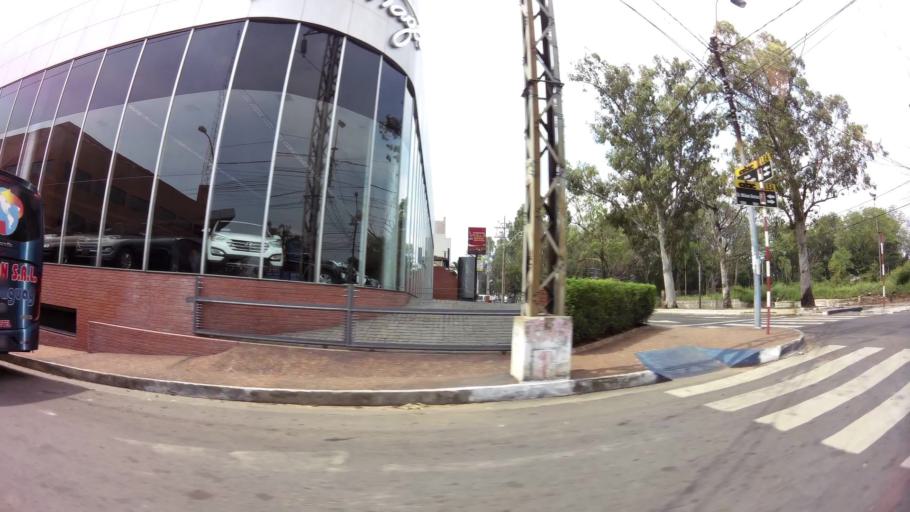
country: PY
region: Asuncion
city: Asuncion
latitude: -25.2921
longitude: -57.5753
